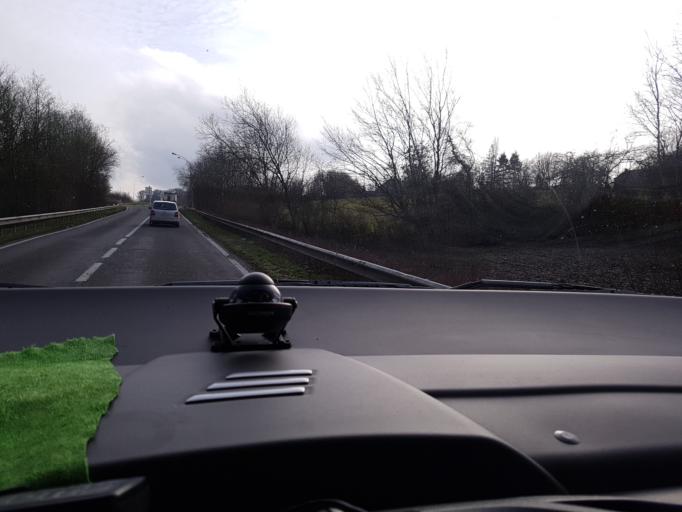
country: FR
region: Nord-Pas-de-Calais
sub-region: Departement du Nord
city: Fourmies
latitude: 50.0147
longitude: 4.0294
